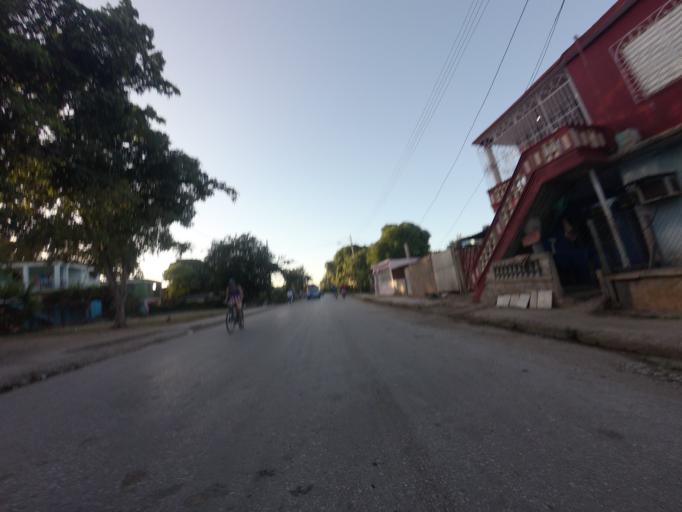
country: CU
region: Ciego de Avila
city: Ciego de Avila
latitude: 21.8313
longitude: -78.7558
